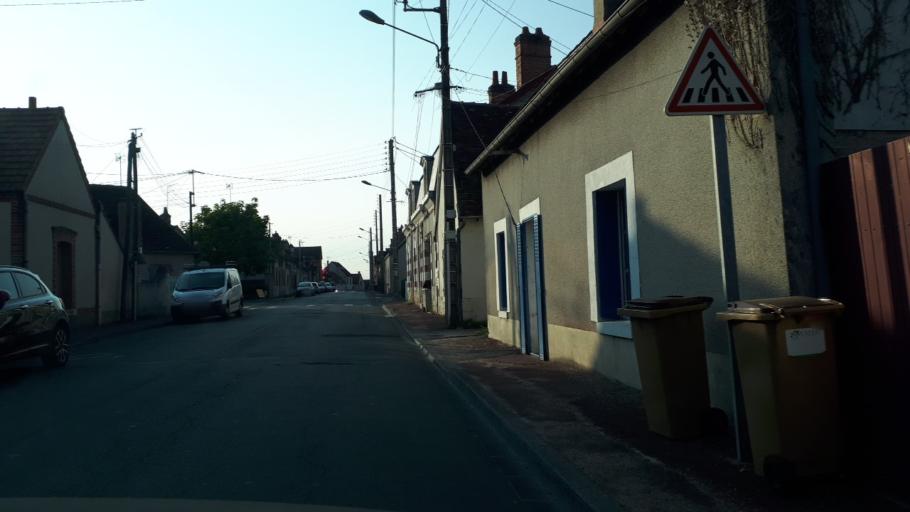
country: FR
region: Centre
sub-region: Departement du Loir-et-Cher
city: Romorantin-Lanthenay
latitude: 47.3613
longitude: 1.7362
